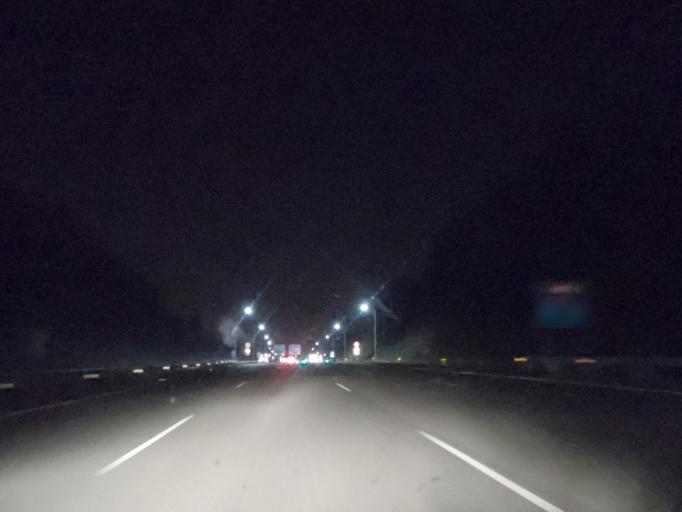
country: ES
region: Galicia
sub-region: Provincia da Coruna
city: Bergondo
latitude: 43.2801
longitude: -8.2682
